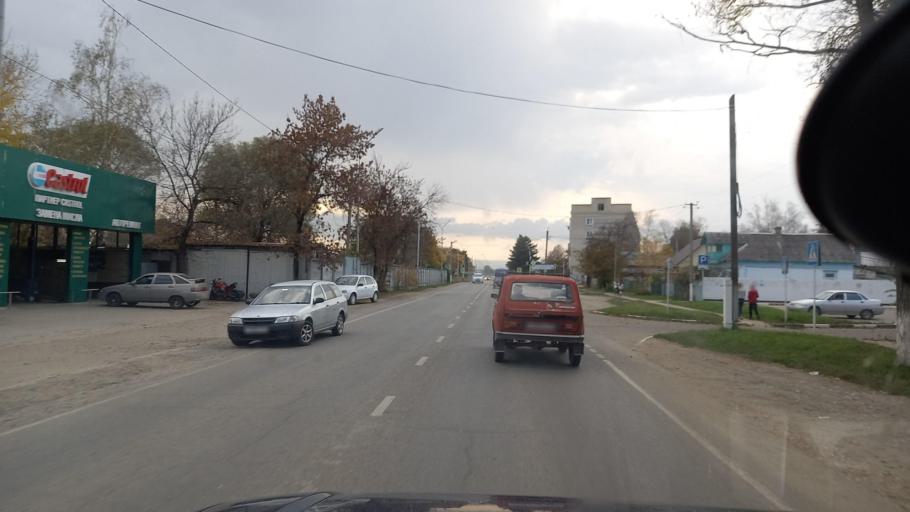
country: RU
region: Krasnodarskiy
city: Mostovskoy
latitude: 44.4038
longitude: 40.7841
